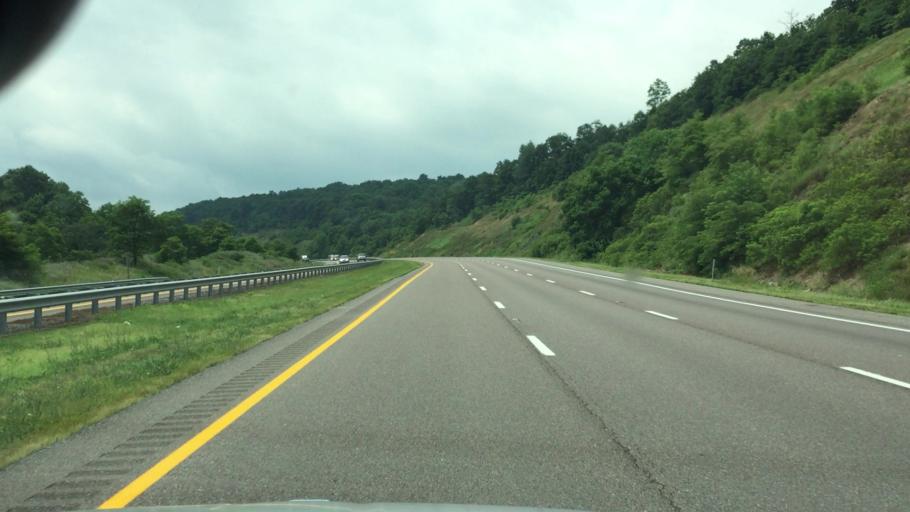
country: US
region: Maryland
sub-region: Allegany County
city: Cumberland
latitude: 39.6954
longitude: -78.5114
